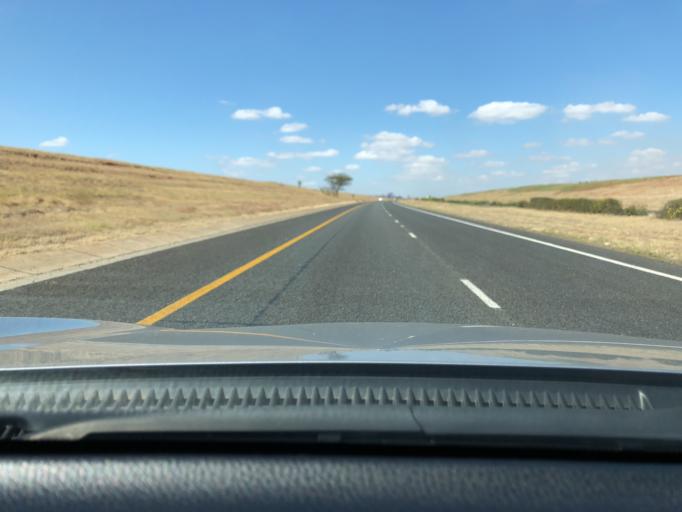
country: ZA
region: KwaZulu-Natal
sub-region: uThukela District Municipality
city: Ladysmith
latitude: -28.7595
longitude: 29.6687
